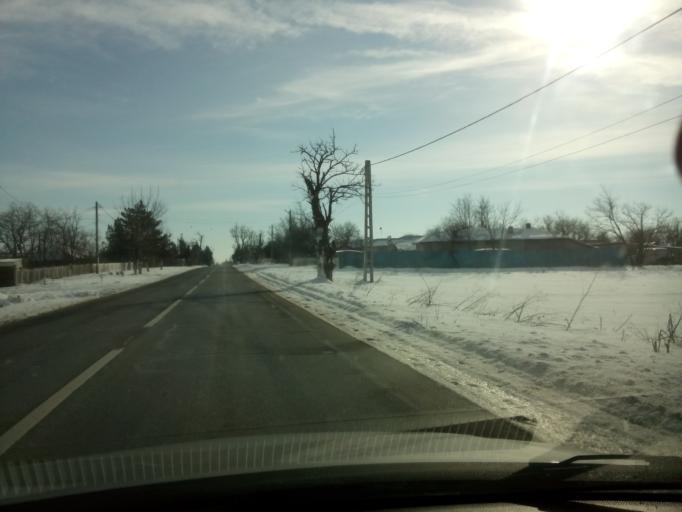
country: RO
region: Calarasi
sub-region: Comuna Frumusani
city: Frumusani
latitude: 44.2962
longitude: 26.3126
